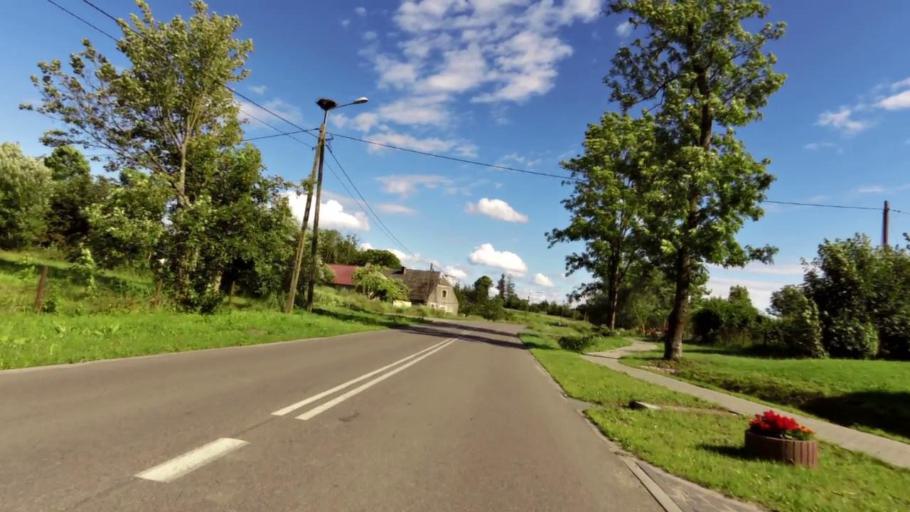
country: PL
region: West Pomeranian Voivodeship
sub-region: Powiat slawienski
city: Slawno
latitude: 54.4586
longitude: 16.7371
